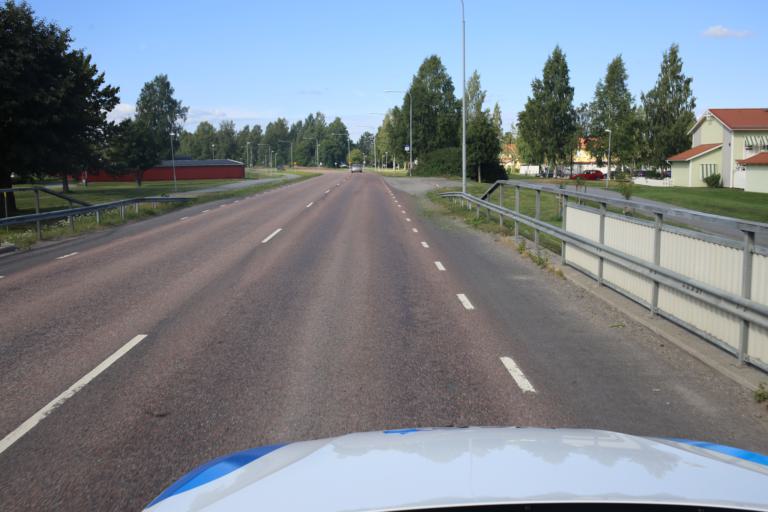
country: SE
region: Vaesterbotten
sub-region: Skelleftea Kommun
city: Skelleftea
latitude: 64.7451
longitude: 20.9782
